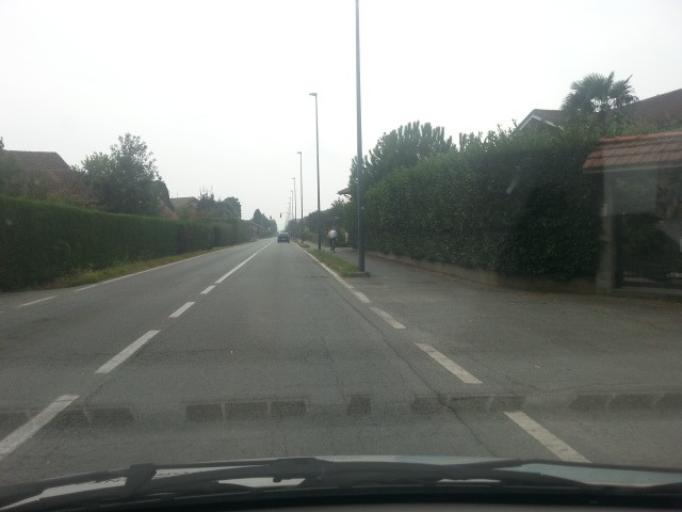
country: IT
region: Piedmont
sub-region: Provincia di Torino
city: Piossasco
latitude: 44.9981
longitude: 7.4673
